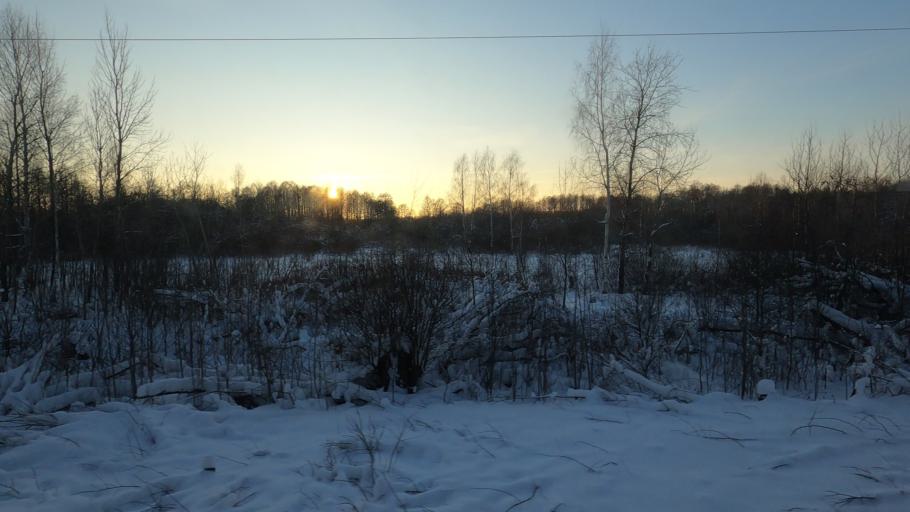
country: RU
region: Moskovskaya
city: Dmitrov
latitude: 56.3888
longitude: 37.5093
